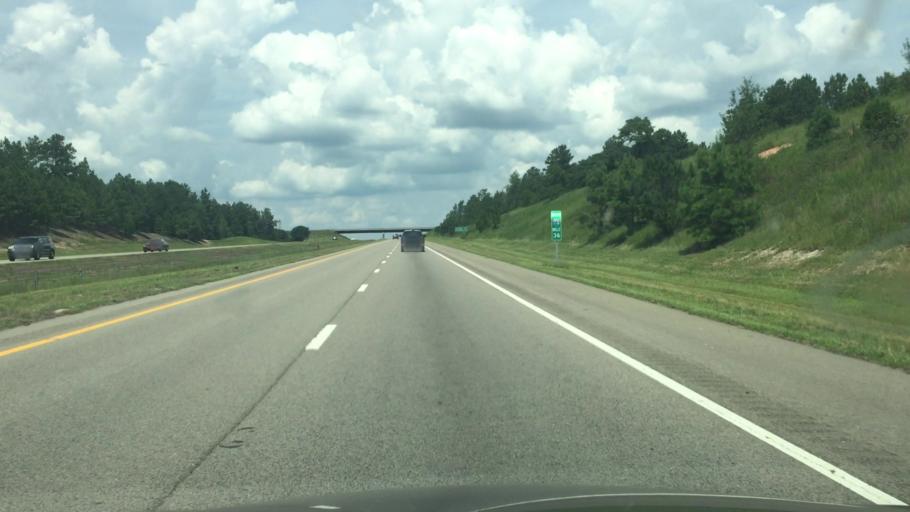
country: US
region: North Carolina
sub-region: Richmond County
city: Ellerbe
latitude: 35.1830
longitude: -79.7168
